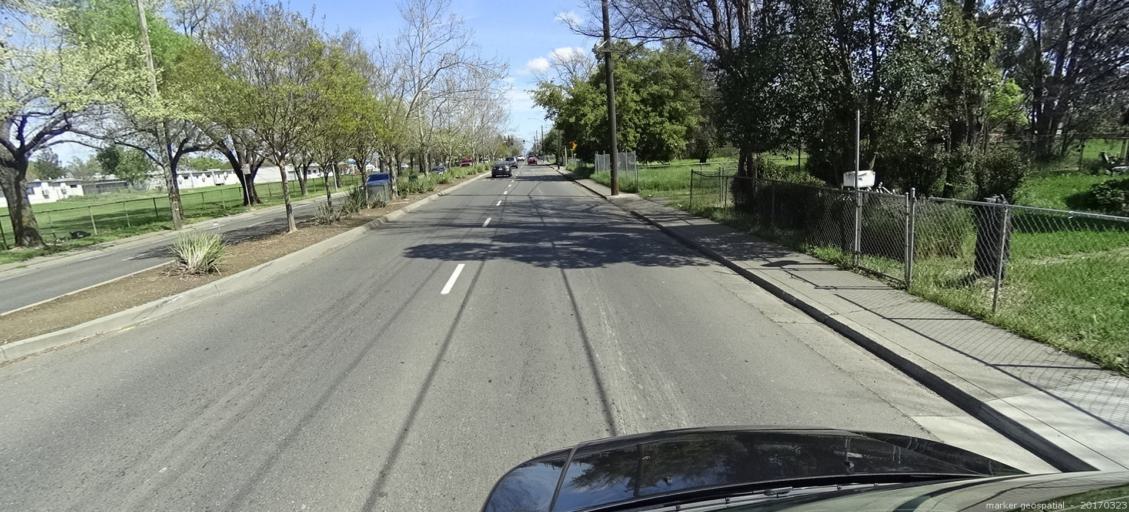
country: US
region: California
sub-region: Sacramento County
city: Florin
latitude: 38.5250
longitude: -121.4193
